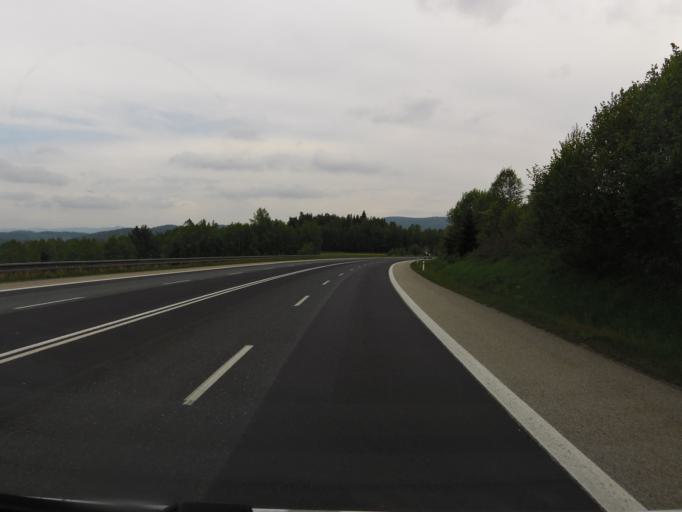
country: DE
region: Bavaria
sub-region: Lower Bavaria
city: Philippsreut
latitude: 48.8938
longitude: 13.7259
